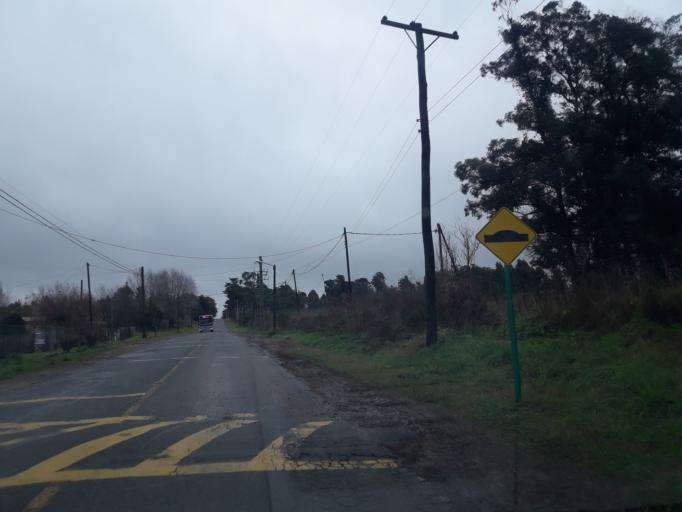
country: AR
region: Buenos Aires
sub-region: Partido de Tandil
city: Tandil
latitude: -37.3273
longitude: -59.1741
